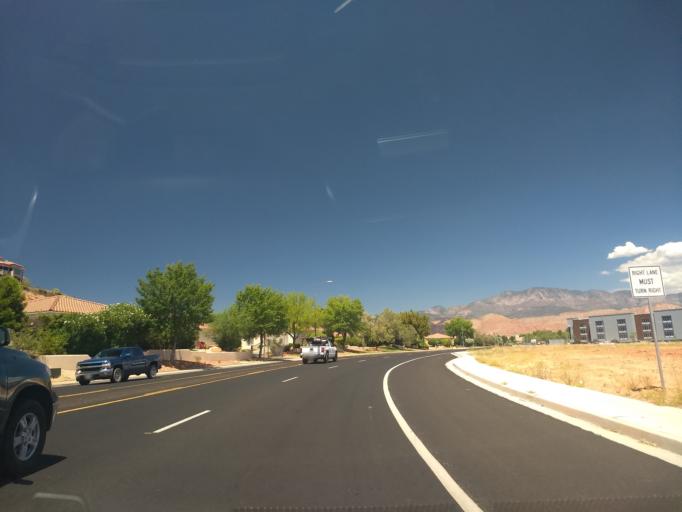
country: US
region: Utah
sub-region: Washington County
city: Washington
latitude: 37.1308
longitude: -113.5269
